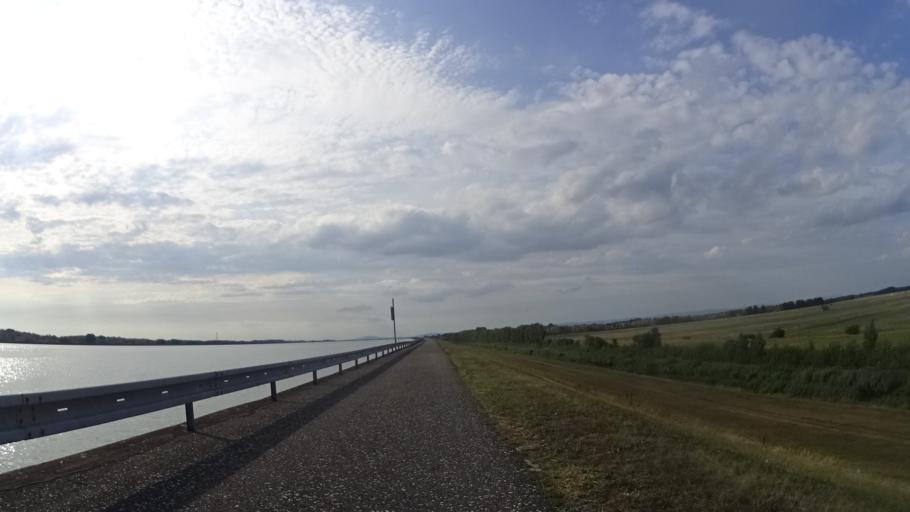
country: HU
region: Gyor-Moson-Sopron
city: Halaszi
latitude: 47.9555
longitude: 17.4315
